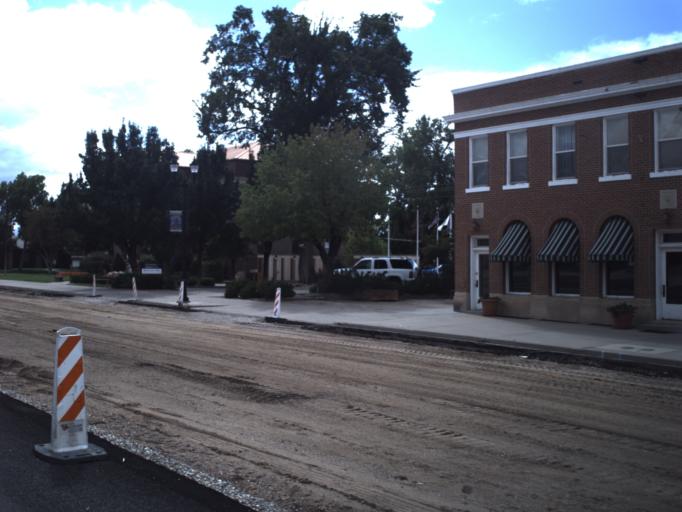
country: US
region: Utah
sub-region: Millard County
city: Fillmore
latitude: 38.9686
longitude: -112.3237
